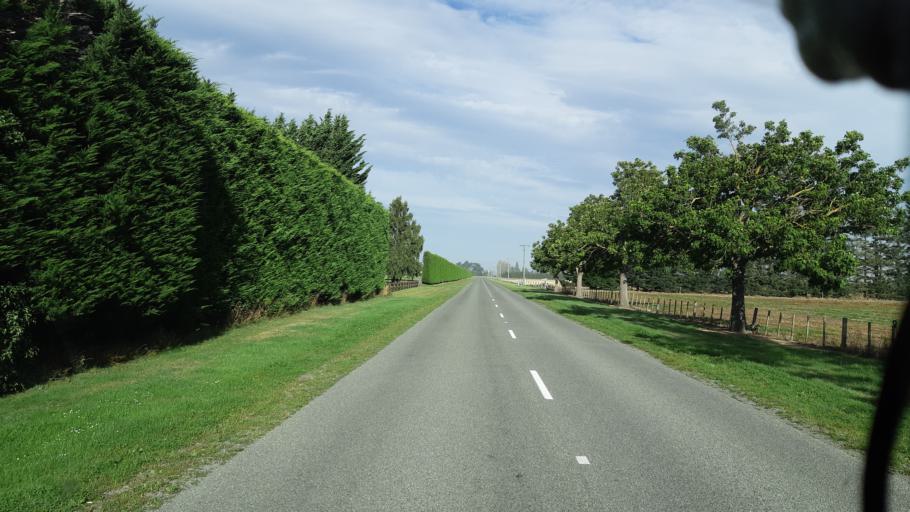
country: NZ
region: Canterbury
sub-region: Ashburton District
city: Rakaia
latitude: -43.6741
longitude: 171.8520
